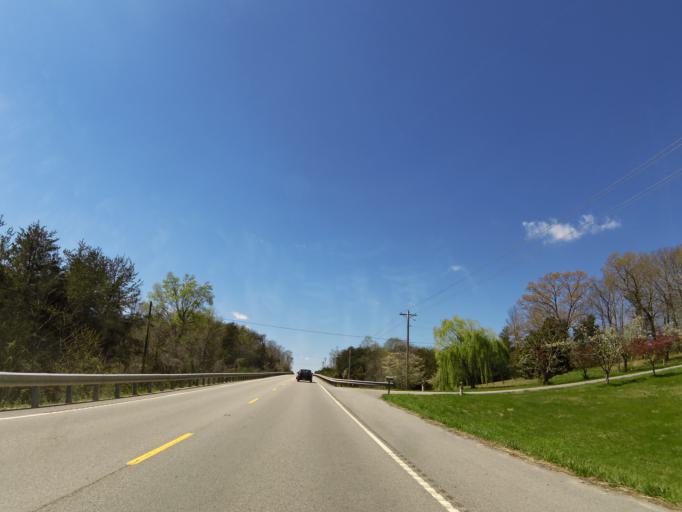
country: US
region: Tennessee
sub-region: White County
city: Sparta
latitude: 35.9632
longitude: -85.6325
